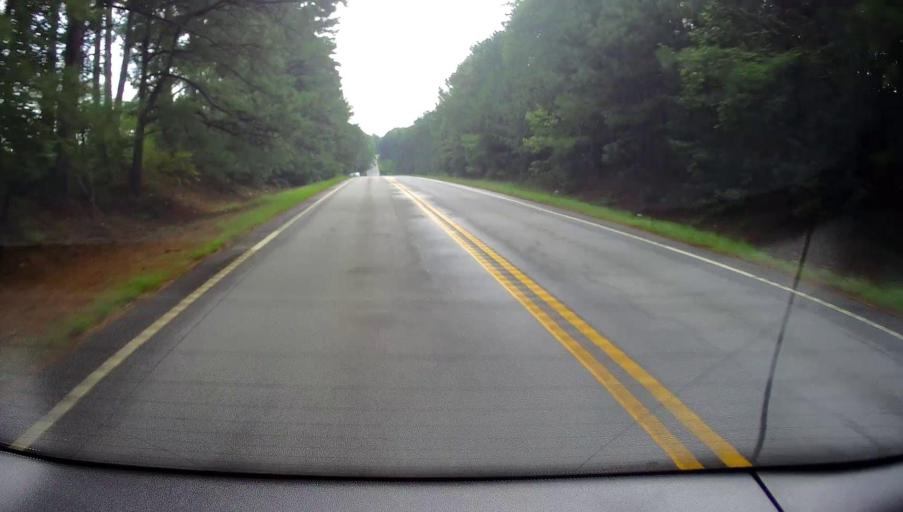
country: US
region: Georgia
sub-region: Coweta County
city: Senoia
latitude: 33.2659
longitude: -84.5548
